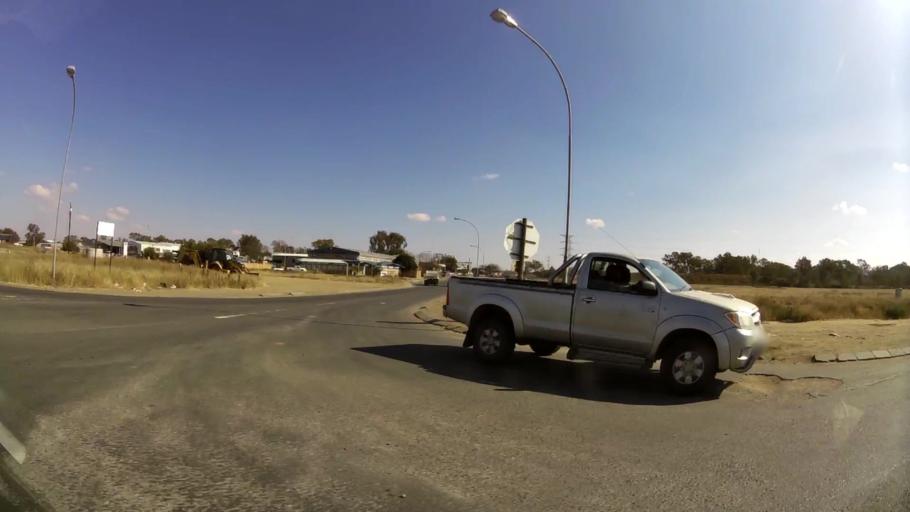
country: ZA
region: Orange Free State
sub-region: Mangaung Metropolitan Municipality
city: Bloemfontein
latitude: -29.1273
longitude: 26.2671
